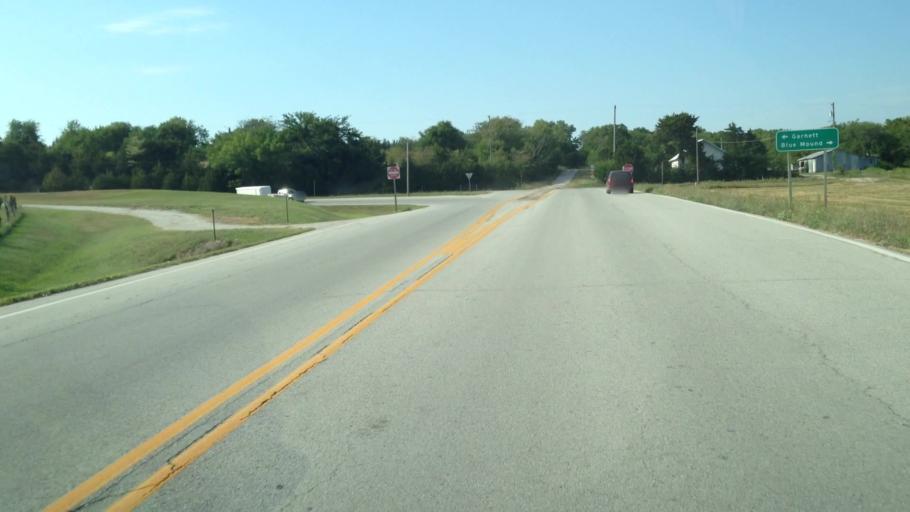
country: US
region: Kansas
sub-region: Anderson County
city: Garnett
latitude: 38.0802
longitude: -95.1694
